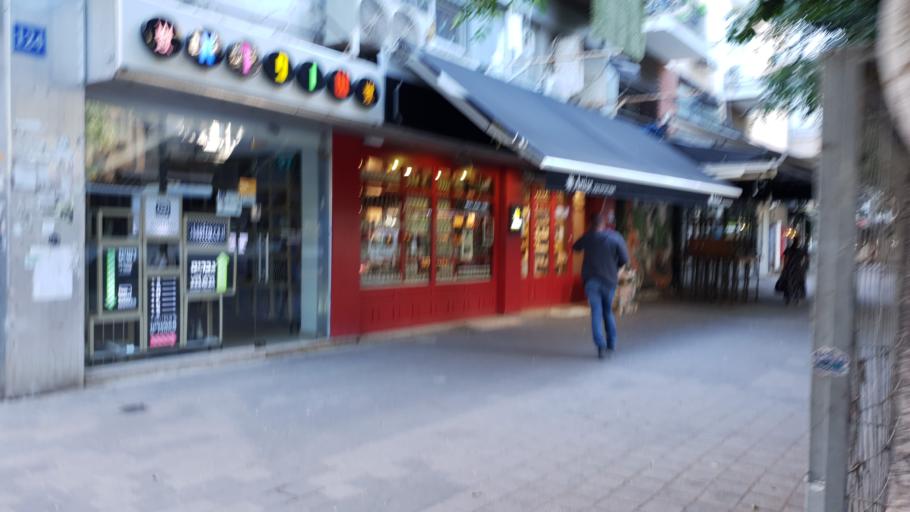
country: IL
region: Tel Aviv
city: Tel Aviv
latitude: 32.0812
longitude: 34.7739
